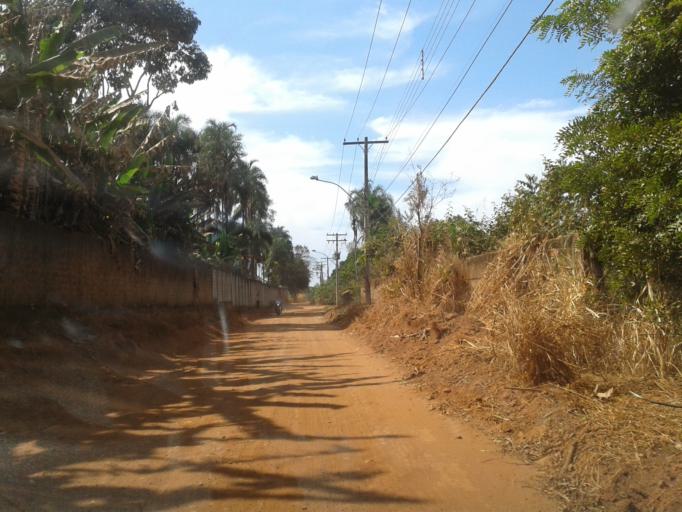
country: BR
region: Goias
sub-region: Goiania
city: Goiania
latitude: -16.6417
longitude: -49.3453
